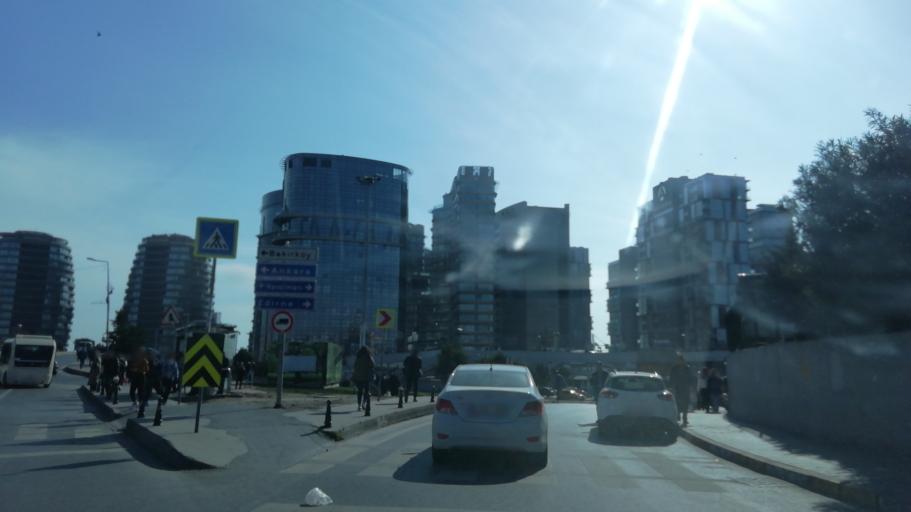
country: TR
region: Istanbul
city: Bahcelievler
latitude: 40.9936
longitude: 28.8353
